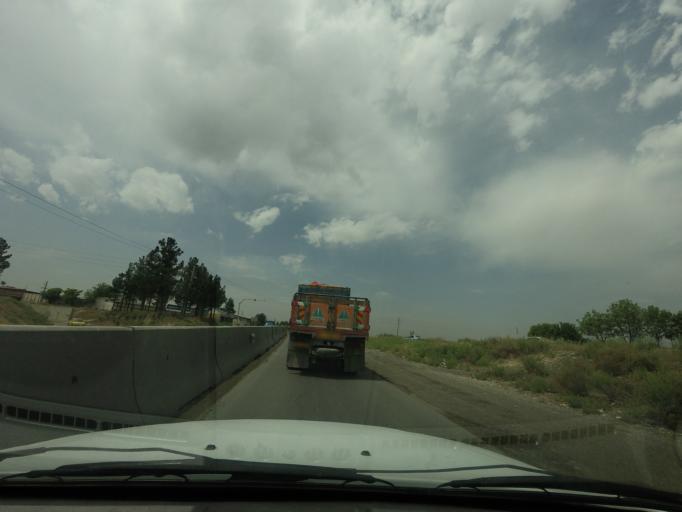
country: IR
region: Tehran
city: Shahrak-e Emam Hasan-e Mojtaba
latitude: 35.5094
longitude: 51.2910
